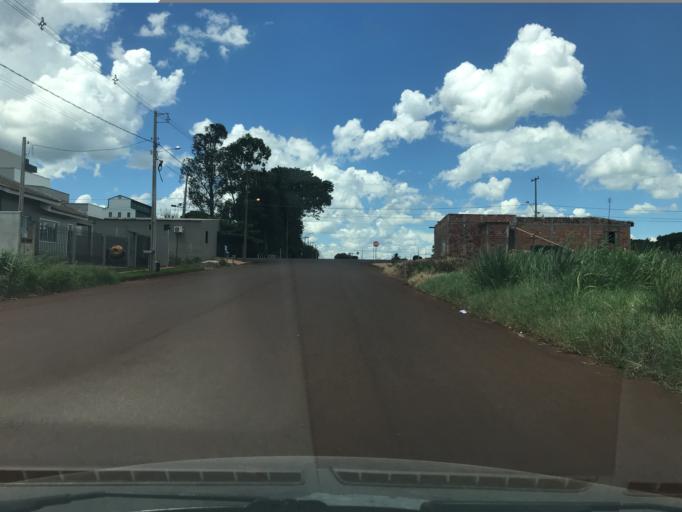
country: BR
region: Parana
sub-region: Palotina
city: Palotina
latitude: -24.2649
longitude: -53.8426
